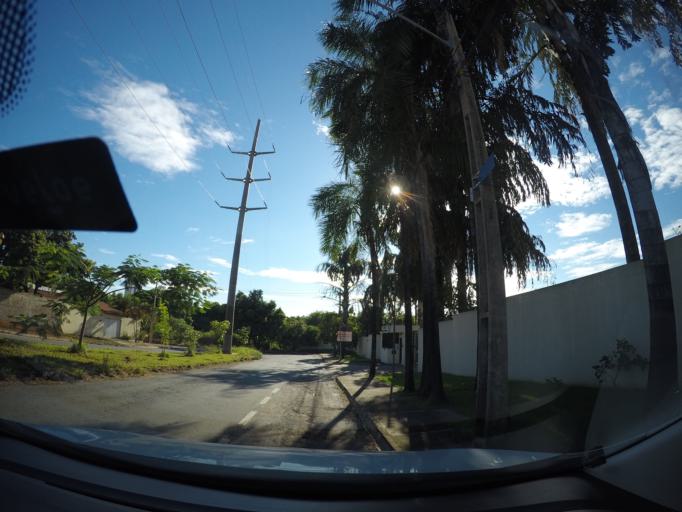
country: BR
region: Goias
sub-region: Goiania
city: Goiania
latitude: -16.7241
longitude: -49.2945
